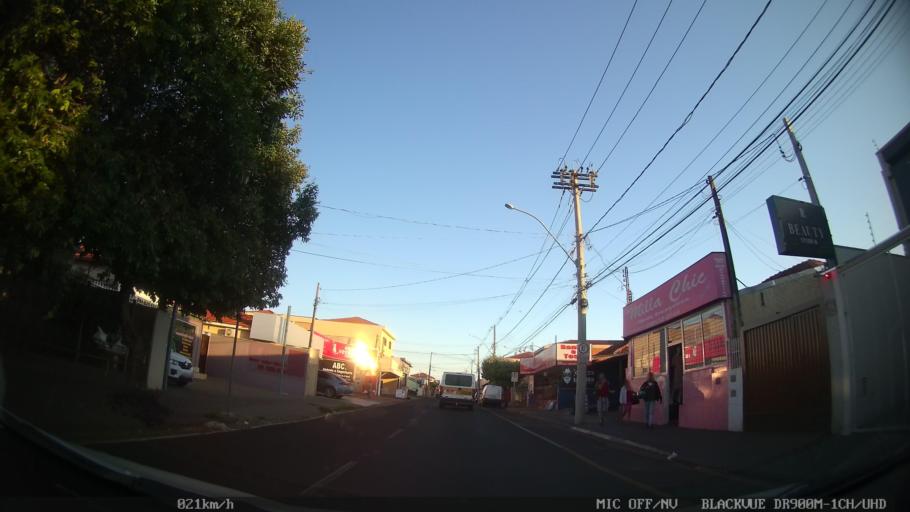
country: BR
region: Sao Paulo
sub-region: Sao Jose Do Rio Preto
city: Sao Jose do Rio Preto
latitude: -20.7902
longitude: -49.3695
